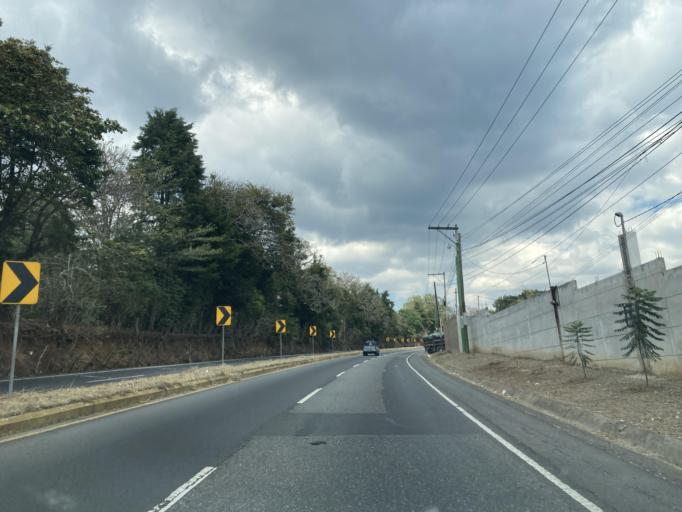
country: GT
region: Guatemala
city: Fraijanes
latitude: 14.4378
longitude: -90.4765
